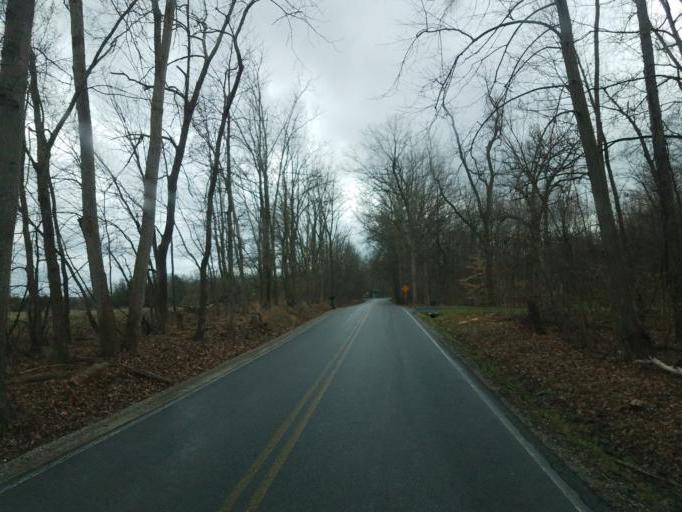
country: US
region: Ohio
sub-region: Delaware County
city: Lewis Center
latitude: 40.2119
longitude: -82.9415
